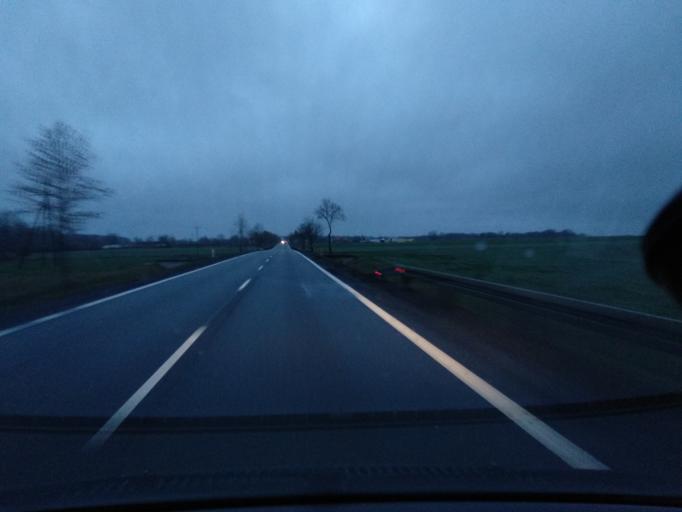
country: PL
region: Lower Silesian Voivodeship
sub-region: Powiat sredzki
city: Malczyce
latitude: 51.1966
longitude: 16.4938
